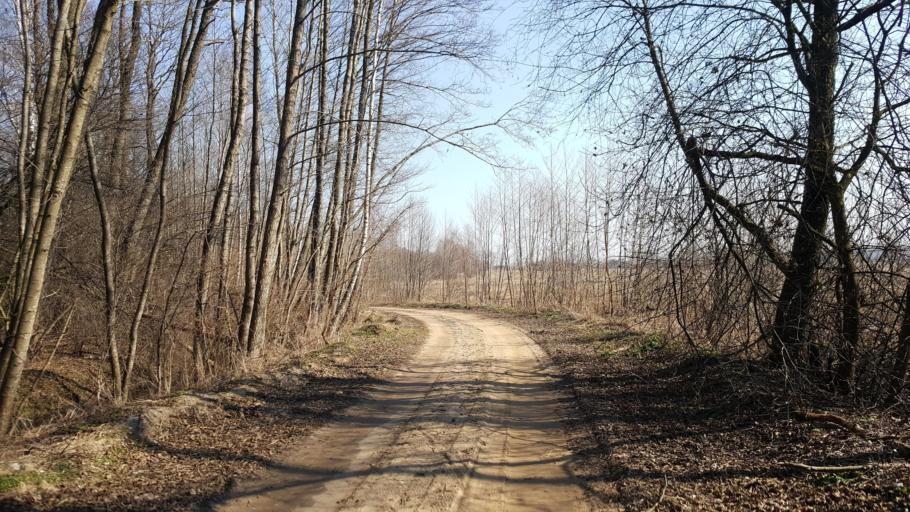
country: BY
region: Brest
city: Kamyanyets
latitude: 52.3656
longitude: 23.7561
